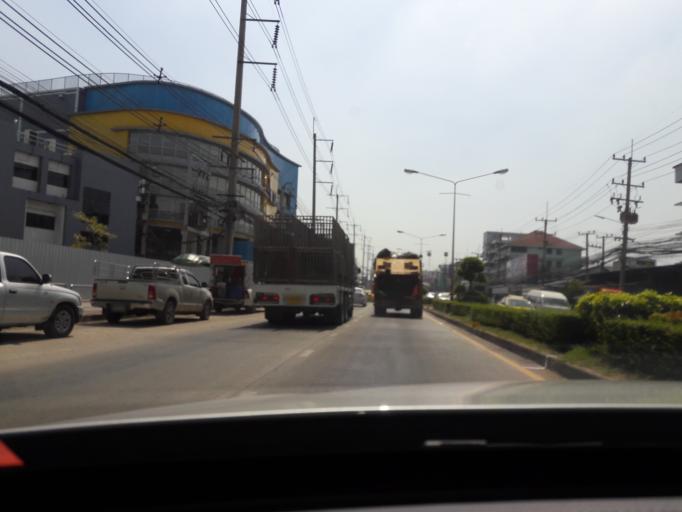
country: TH
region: Samut Sakhon
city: Samut Sakhon
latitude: 13.5710
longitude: 100.2722
